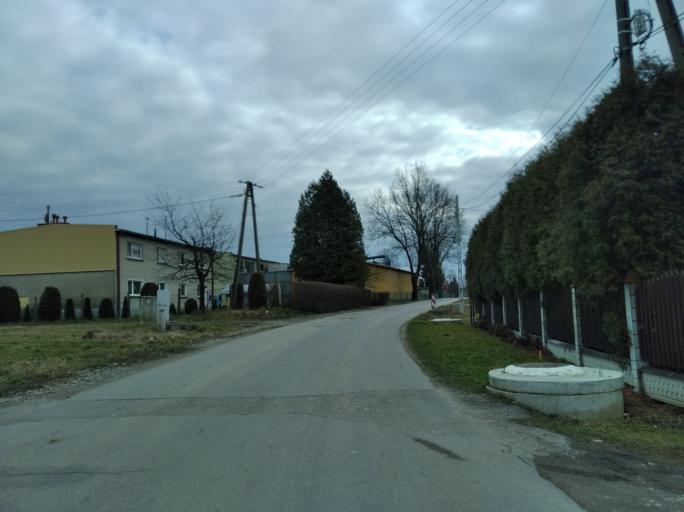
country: PL
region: Subcarpathian Voivodeship
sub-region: Powiat strzyzowski
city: Frysztak
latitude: 49.8378
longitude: 21.6162
